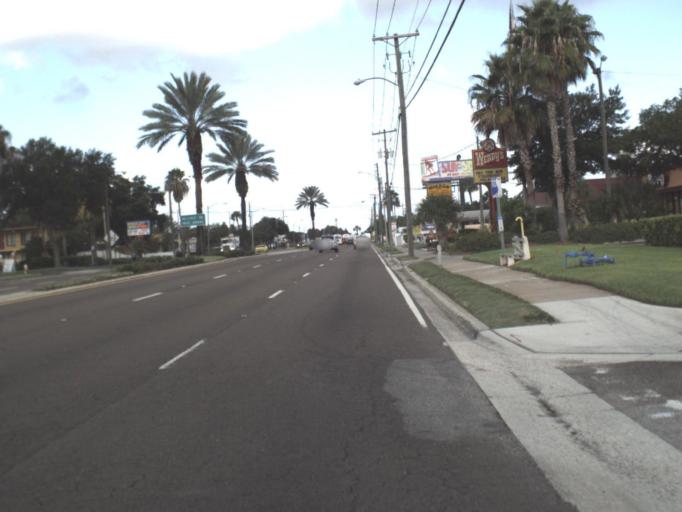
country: US
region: Florida
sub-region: Pinellas County
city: South Highpoint
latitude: 27.9606
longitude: -82.7418
